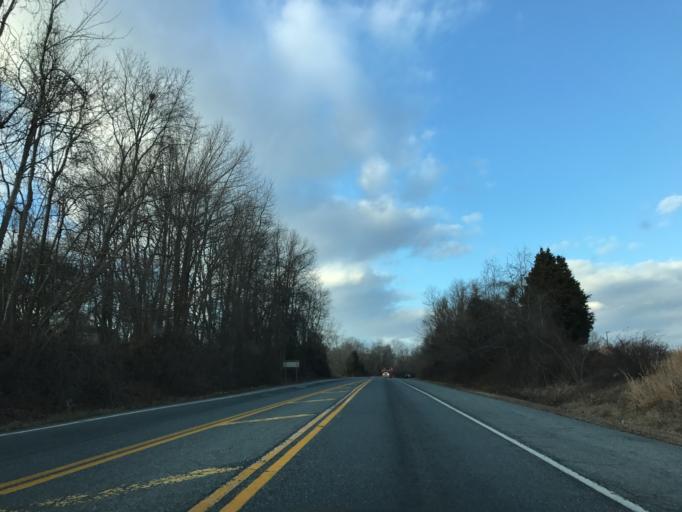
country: US
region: Maryland
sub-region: Cecil County
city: North East
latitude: 39.6424
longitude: -75.9585
